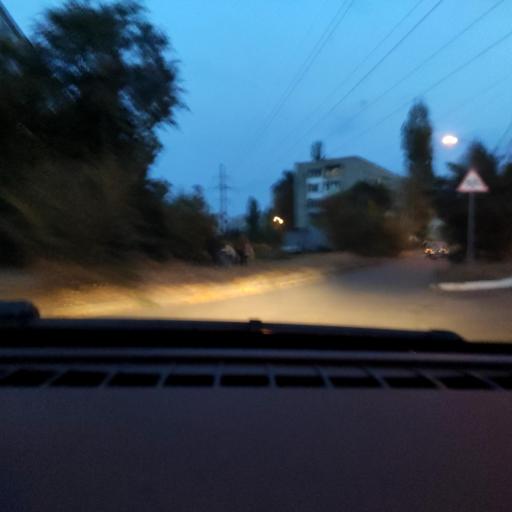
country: RU
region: Voronezj
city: Voronezh
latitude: 51.7187
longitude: 39.2670
